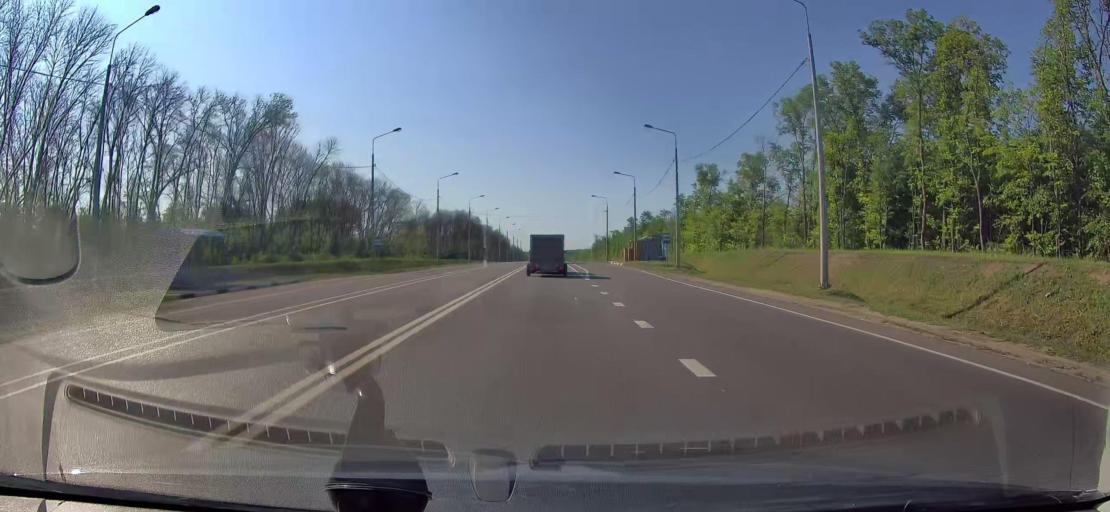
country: RU
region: Orjol
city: Kromy
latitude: 52.6309
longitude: 35.7535
